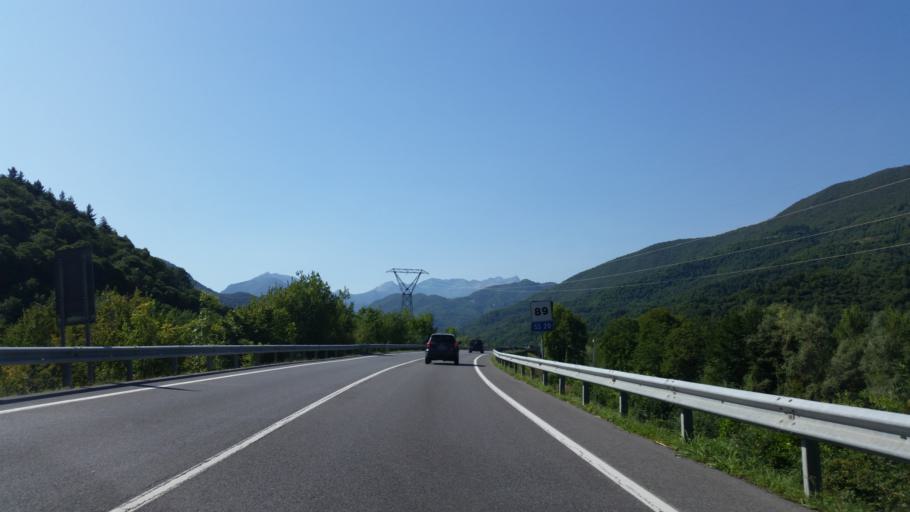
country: IT
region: Piedmont
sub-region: Provincia di Cuneo
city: Robilante
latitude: 44.2990
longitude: 7.5164
